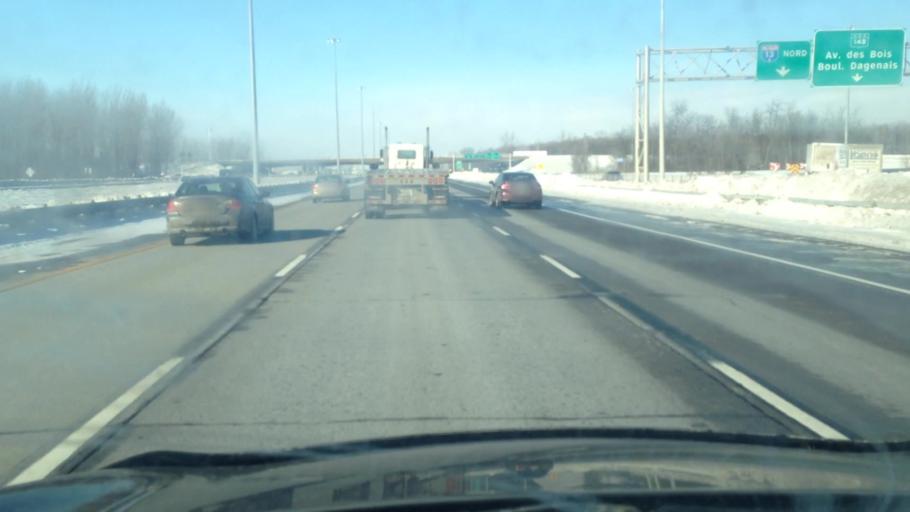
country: CA
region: Quebec
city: Dollard-Des Ormeaux
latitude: 45.5517
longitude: -73.8053
